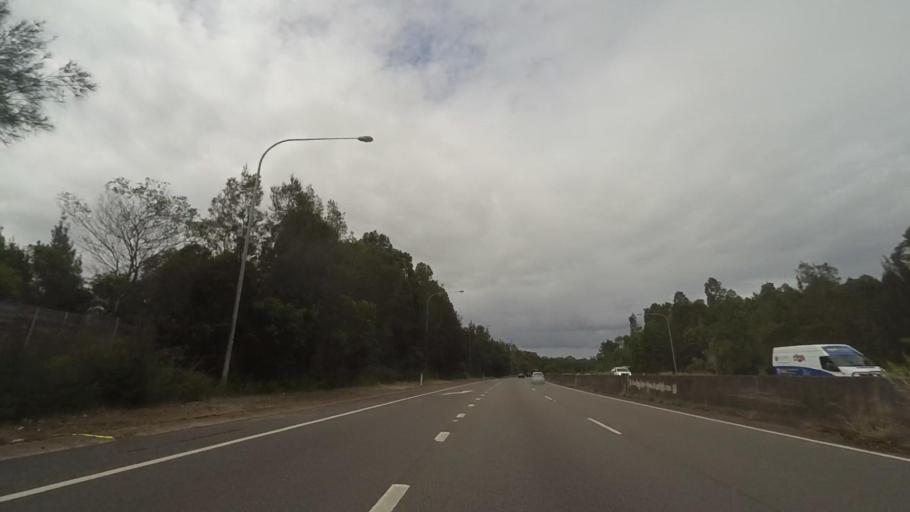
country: AU
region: New South Wales
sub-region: Port Stephens Shire
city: Raymond Terrace
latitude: -32.7510
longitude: 151.7666
